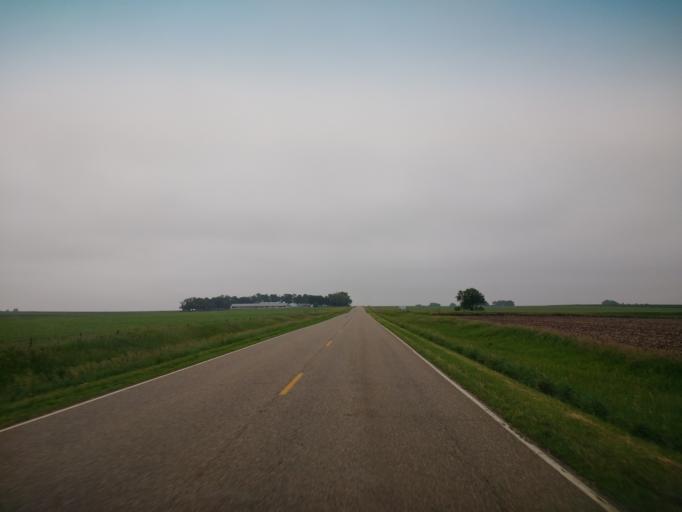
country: US
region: Iowa
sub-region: Sioux County
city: Alton
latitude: 42.9854
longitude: -95.8992
